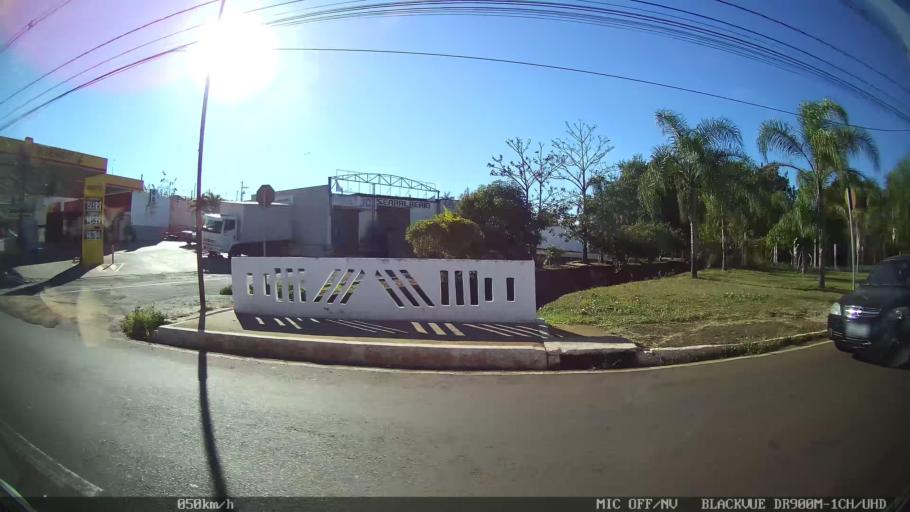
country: BR
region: Sao Paulo
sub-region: Franca
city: Franca
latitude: -20.5527
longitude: -47.3964
